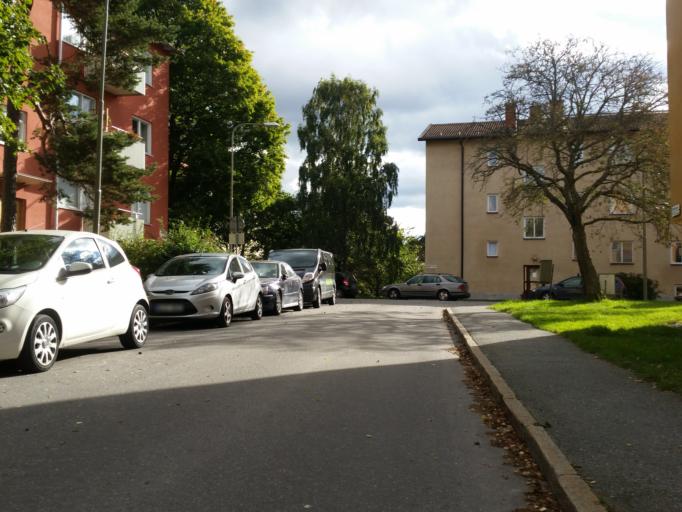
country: SE
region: Stockholm
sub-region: Stockholms Kommun
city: Arsta
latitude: 59.2926
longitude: 18.0988
